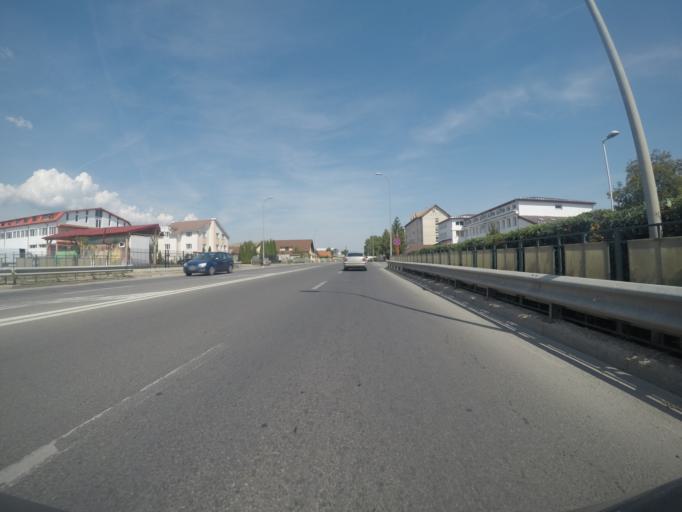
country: RO
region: Alba
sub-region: Municipiul Alba Iulia
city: Barabant
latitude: 46.0902
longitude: 23.5938
